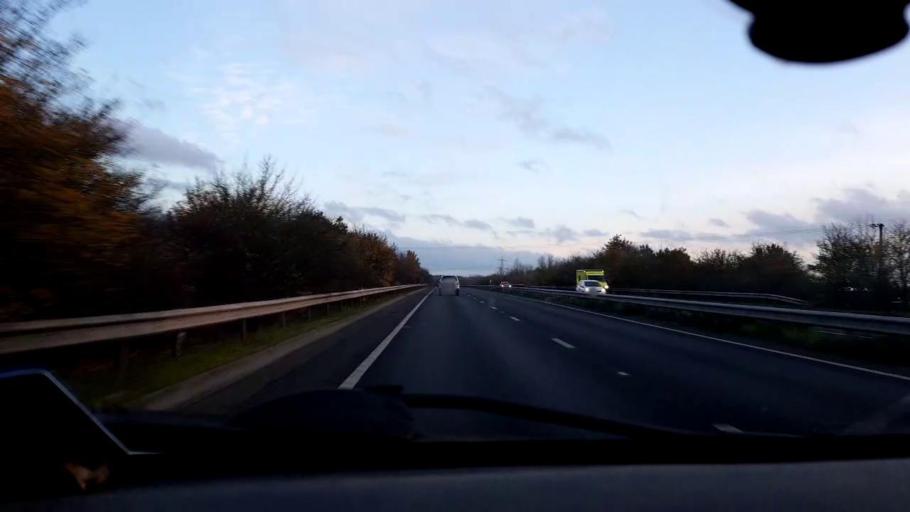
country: GB
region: England
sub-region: Norfolk
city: Cringleford
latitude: 52.6054
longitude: 1.2223
